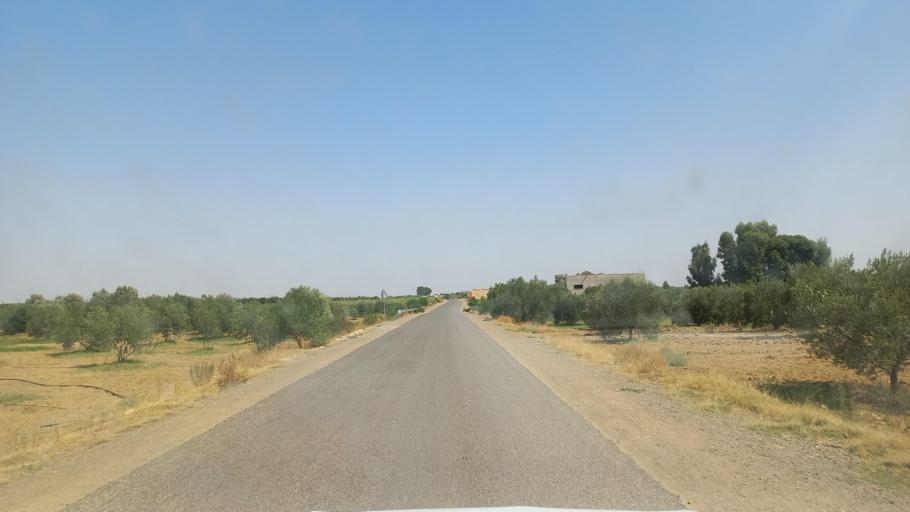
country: TN
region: Al Qasrayn
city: Kasserine
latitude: 35.2356
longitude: 9.0382
